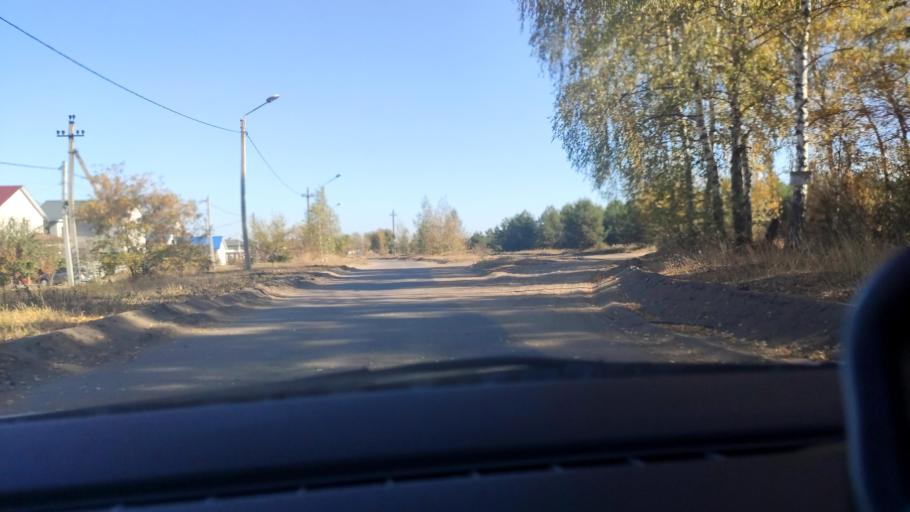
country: RU
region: Voronezj
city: Pridonskoy
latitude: 51.6275
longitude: 39.0918
